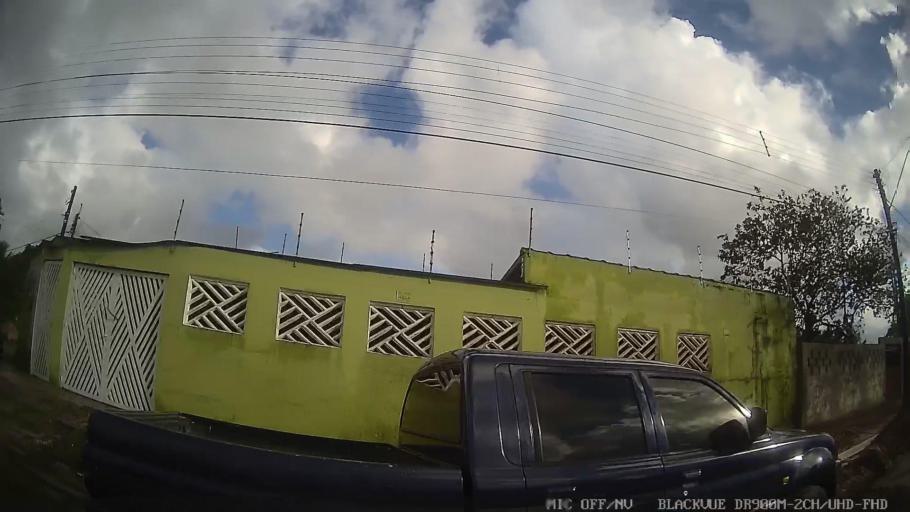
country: BR
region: Sao Paulo
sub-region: Itanhaem
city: Itanhaem
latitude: -24.1726
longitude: -46.8482
